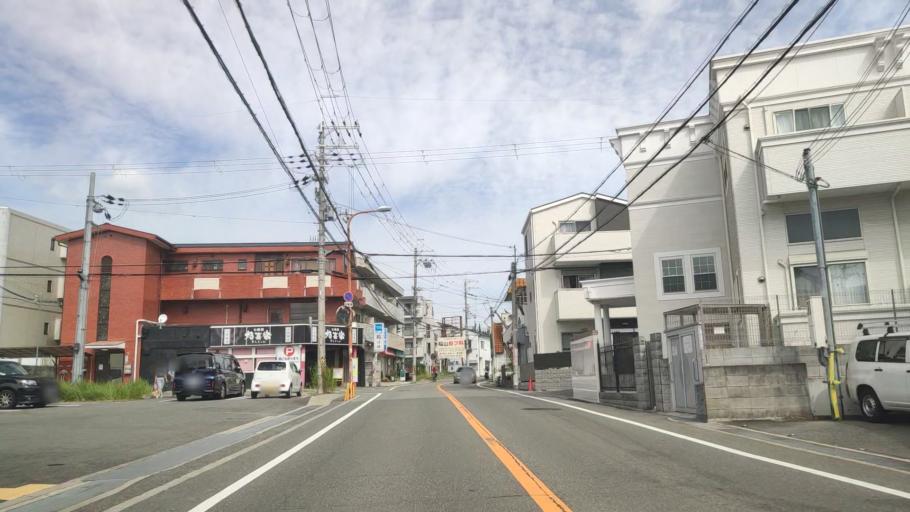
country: JP
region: Osaka
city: Toyonaka
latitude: 34.8005
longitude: 135.4633
